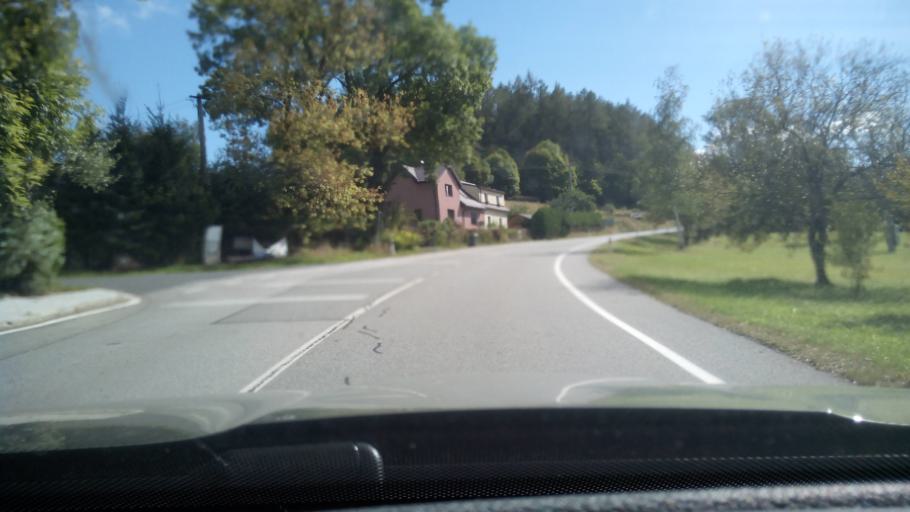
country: CZ
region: Jihocesky
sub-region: Okres Prachatice
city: Zdikov
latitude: 49.0814
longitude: 13.7010
